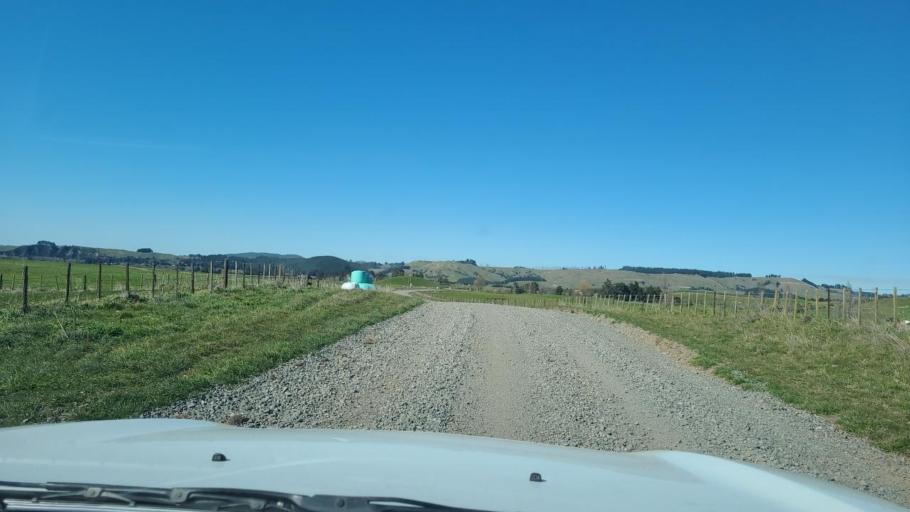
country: NZ
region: Hawke's Bay
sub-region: Napier City
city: Taradale
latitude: -39.4509
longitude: 176.5638
